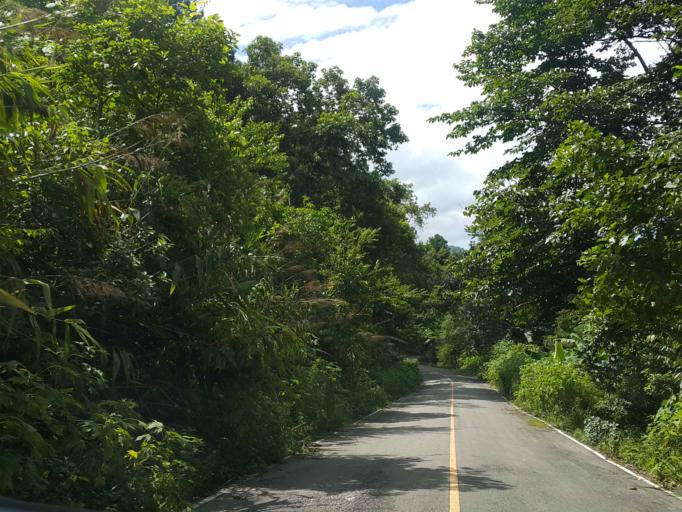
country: TH
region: Chiang Mai
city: Mae Chaem
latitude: 18.5246
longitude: 98.5222
